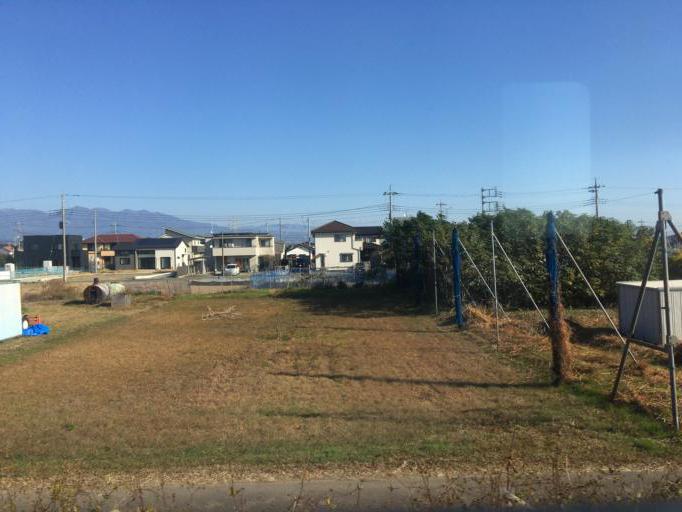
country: JP
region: Gunma
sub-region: Sawa-gun
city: Tamamura
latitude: 36.3644
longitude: 139.1208
